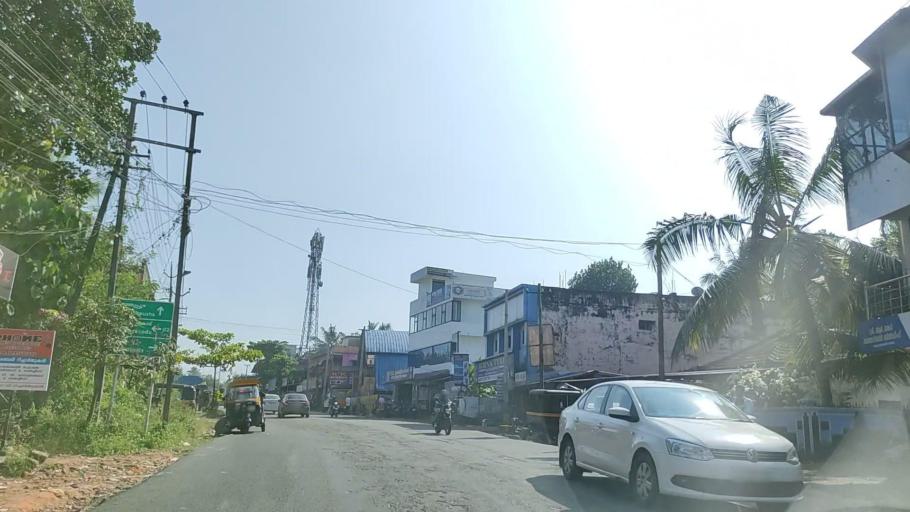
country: IN
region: Kerala
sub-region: Kollam
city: Punalur
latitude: 8.9296
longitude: 76.9303
